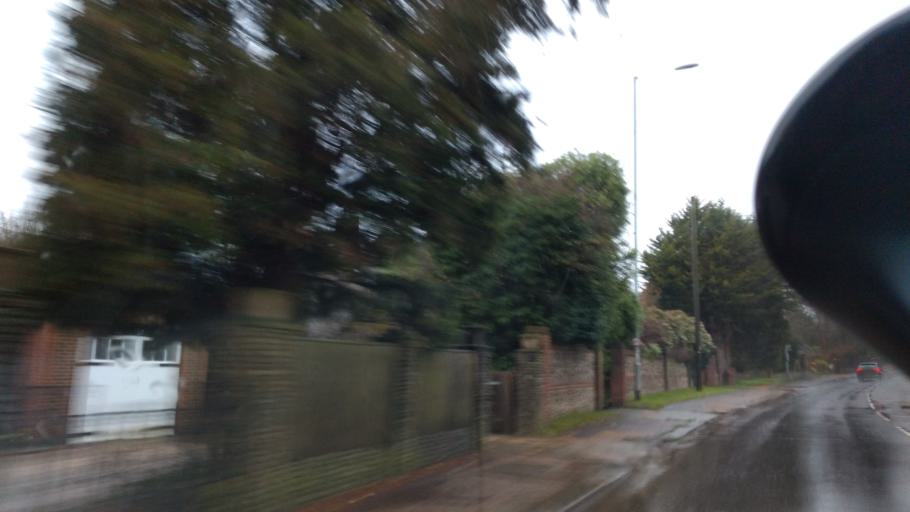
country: GB
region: England
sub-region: West Sussex
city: Broadwater
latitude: 50.8364
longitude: -0.3858
